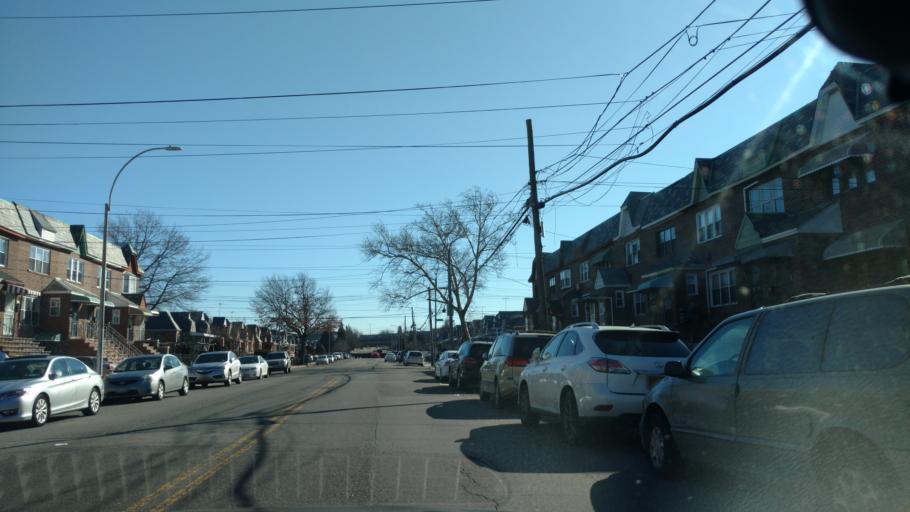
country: US
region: New York
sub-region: Kings County
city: East New York
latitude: 40.7313
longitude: -73.8843
